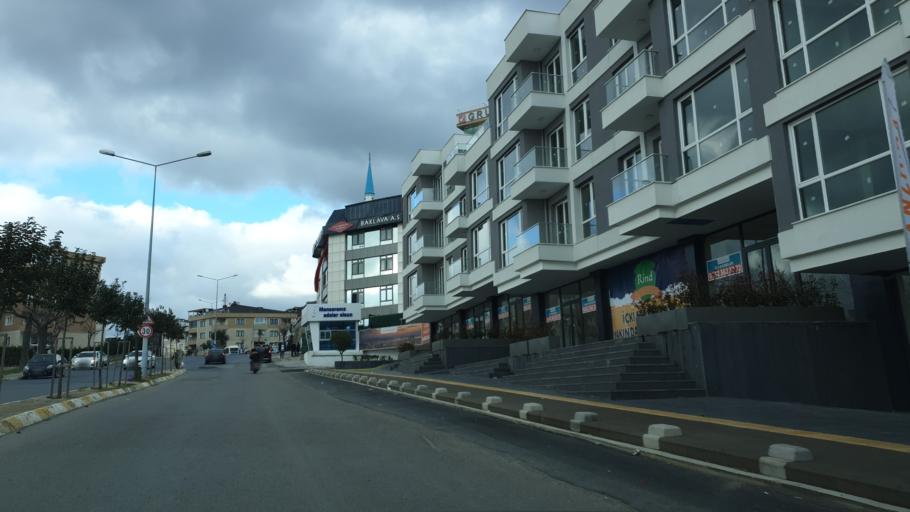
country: TR
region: Istanbul
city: Pendik
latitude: 40.9032
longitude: 29.2470
